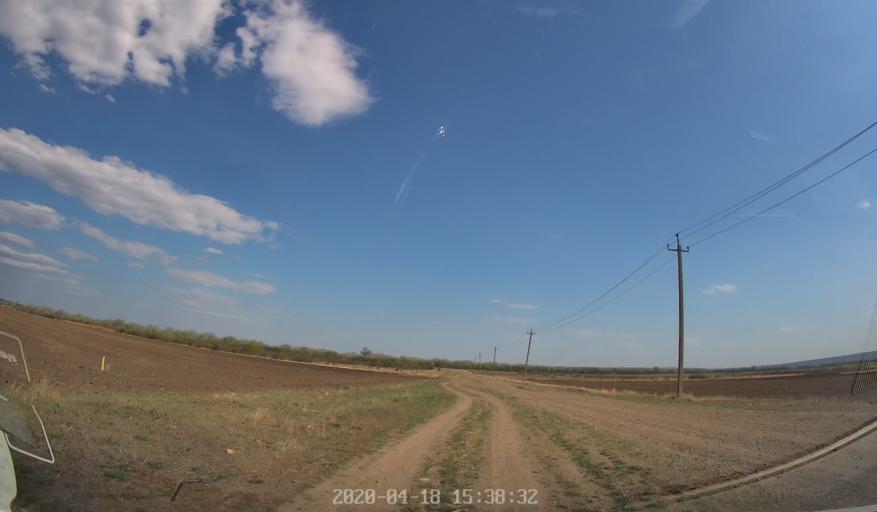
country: MD
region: Chisinau
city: Vadul lui Voda
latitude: 47.1483
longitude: 29.0859
